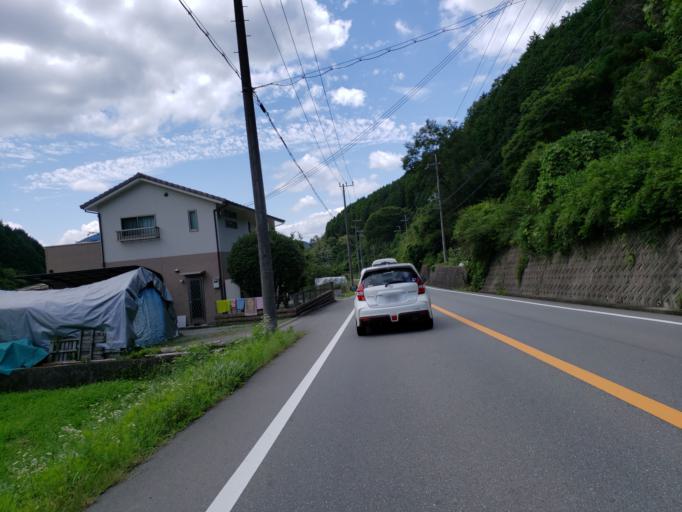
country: JP
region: Hyogo
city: Yamazakicho-nakabirose
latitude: 34.9861
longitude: 134.6080
